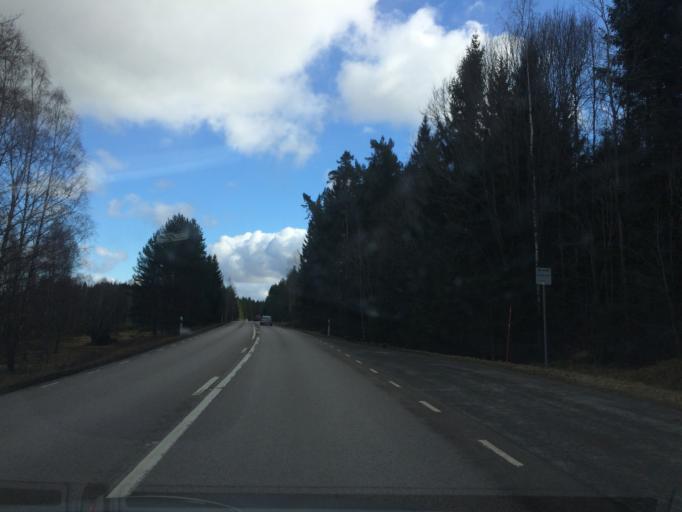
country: SE
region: Vaestra Goetaland
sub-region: Skara Kommun
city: Skara
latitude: 58.3127
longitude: 13.4492
